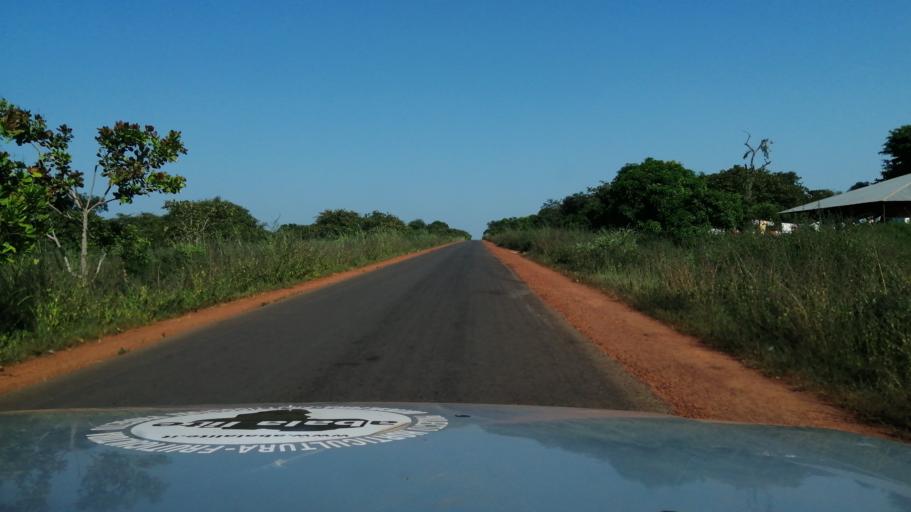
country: GW
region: Bissau
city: Bissau
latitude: 11.9588
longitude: -15.5261
